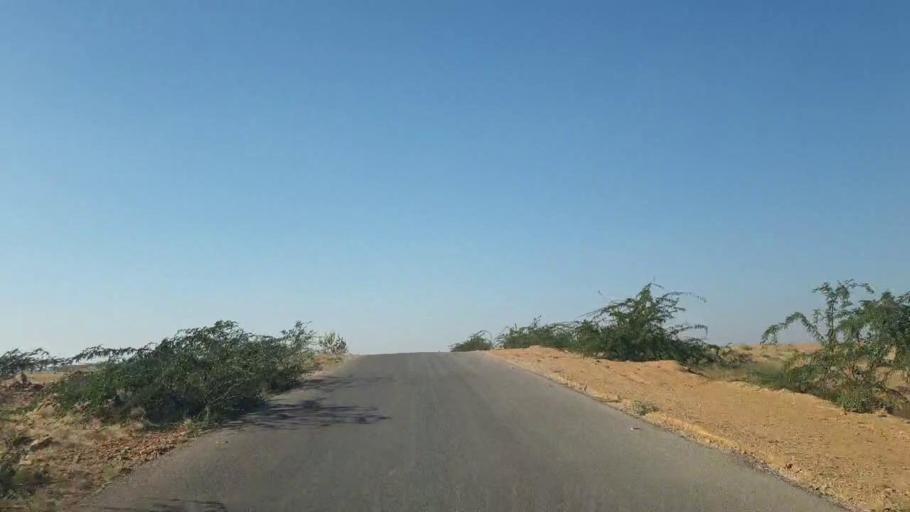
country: PK
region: Sindh
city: Malir Cantonment
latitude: 25.2817
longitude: 67.5826
